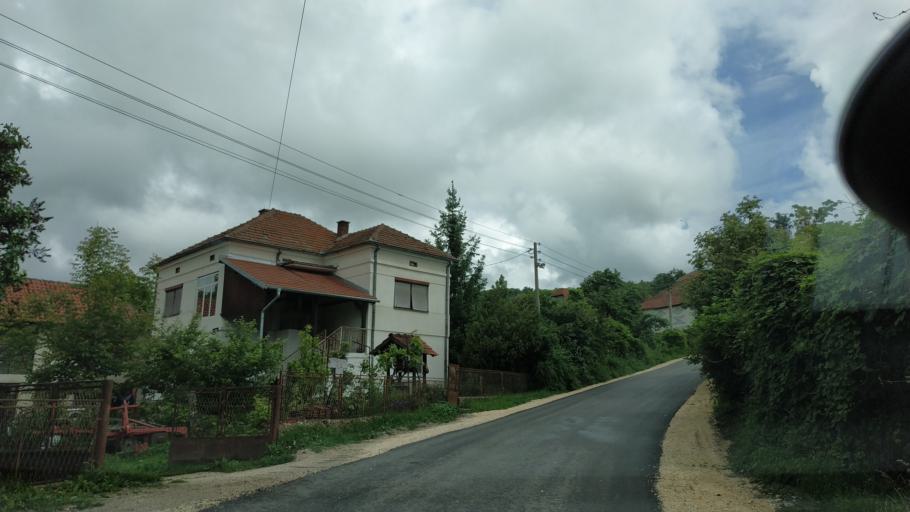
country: RS
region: Central Serbia
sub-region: Zajecarski Okrug
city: Soko Banja
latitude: 43.6785
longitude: 21.9154
